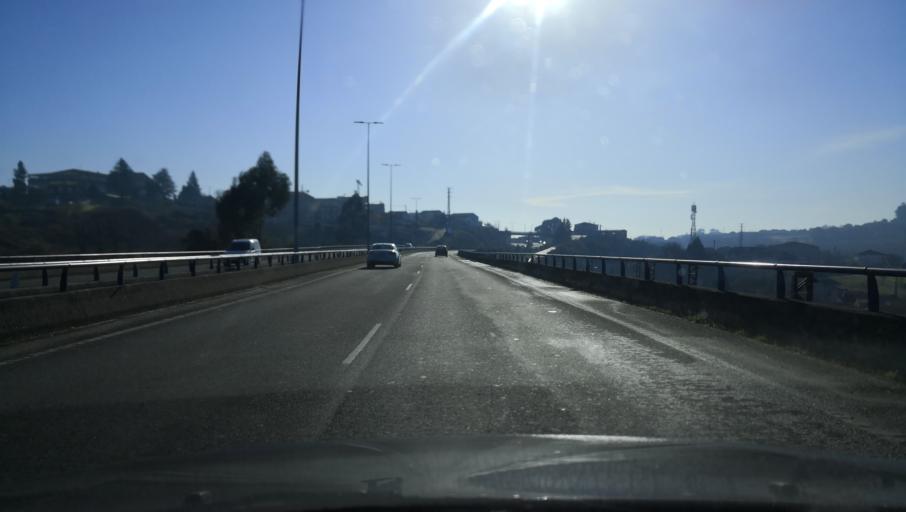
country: ES
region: Galicia
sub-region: Provincia da Coruna
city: Santiago de Compostela
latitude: 42.8630
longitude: -8.5503
